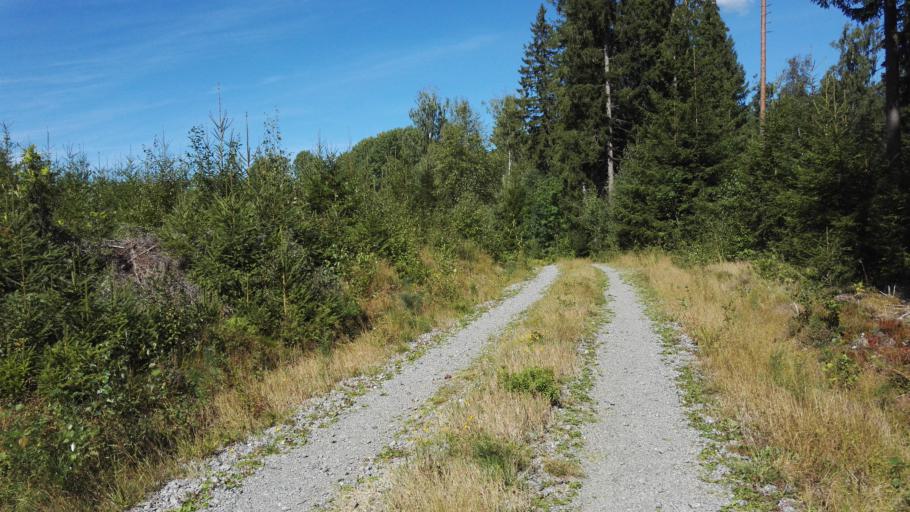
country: SE
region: Joenkoeping
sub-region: Vetlanda Kommun
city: Landsbro
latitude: 57.3253
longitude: 14.8545
